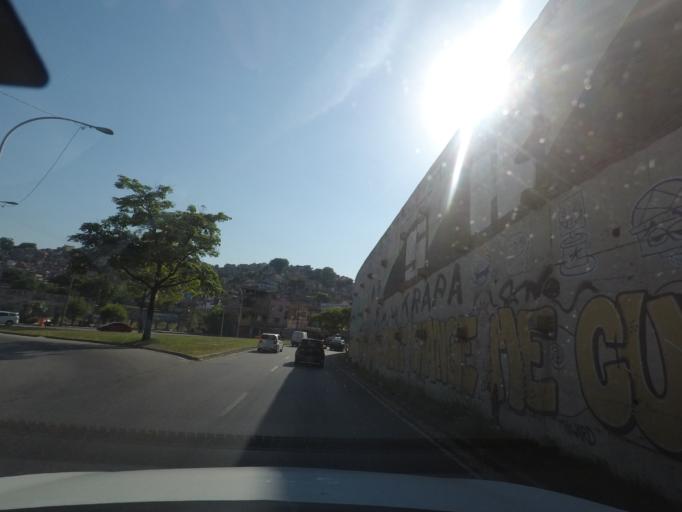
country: BR
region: Rio de Janeiro
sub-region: Rio De Janeiro
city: Rio de Janeiro
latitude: -22.9061
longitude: -43.2414
